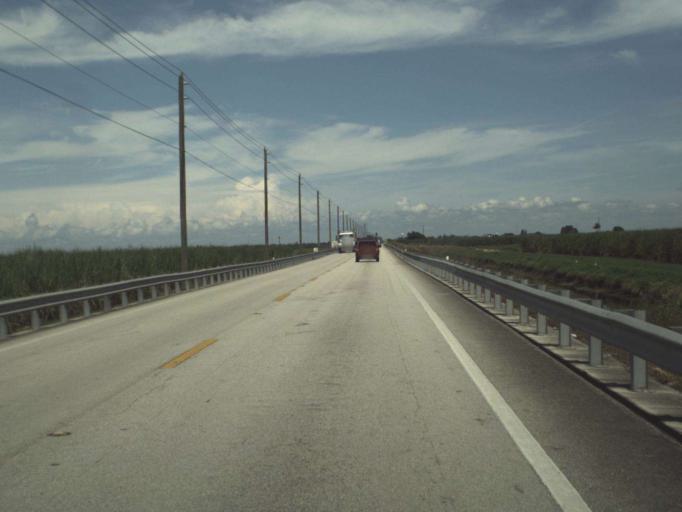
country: US
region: Florida
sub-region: Palm Beach County
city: Pahokee
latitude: 26.7776
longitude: -80.6533
